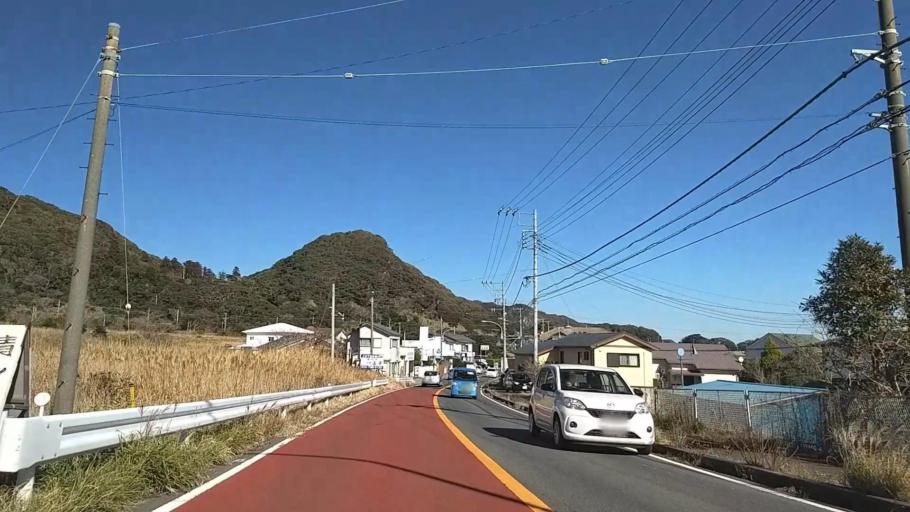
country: JP
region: Chiba
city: Kawaguchi
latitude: 35.0619
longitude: 140.0737
